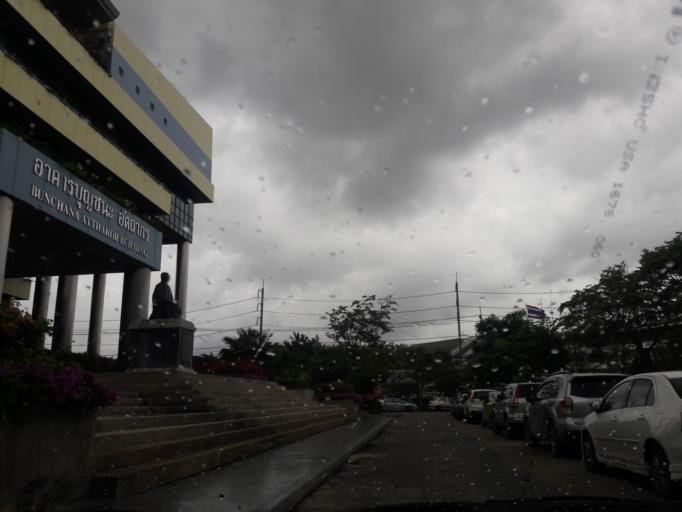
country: TH
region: Bangkok
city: Bang Kapi
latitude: 13.7690
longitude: 100.6529
